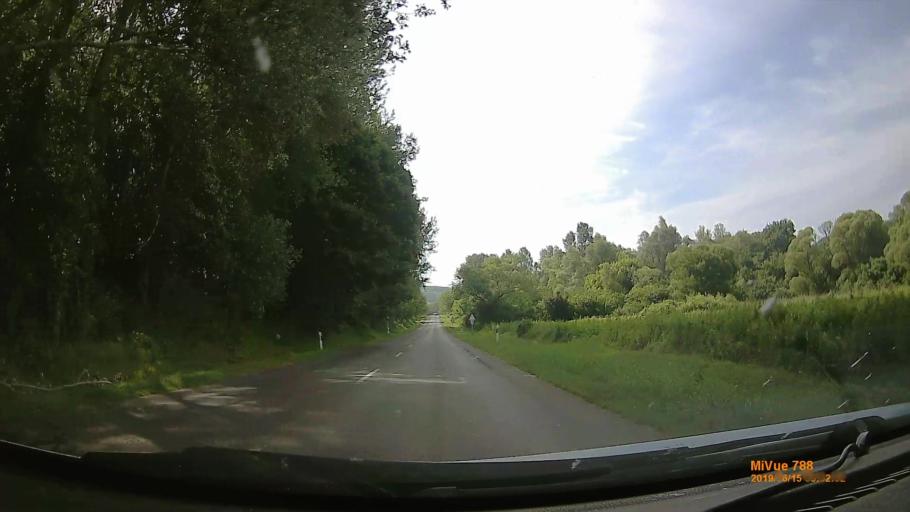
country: HU
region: Tolna
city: Iregszemcse
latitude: 46.7603
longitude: 18.1579
